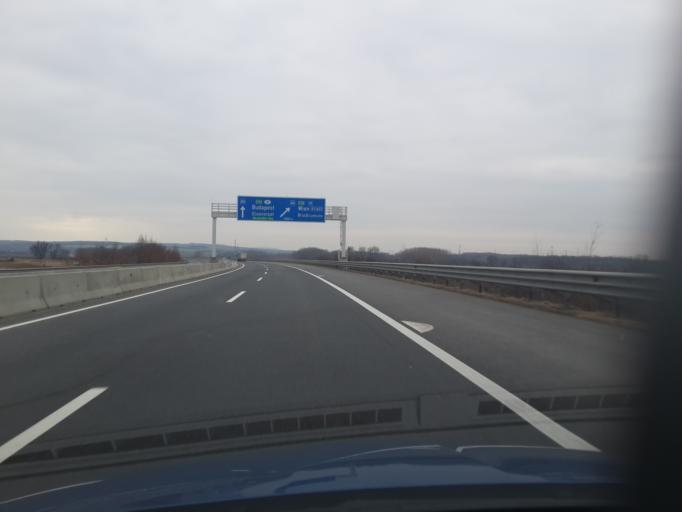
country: AT
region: Burgenland
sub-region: Politischer Bezirk Neusiedl am See
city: Parndorf
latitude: 48.0283
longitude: 16.8560
